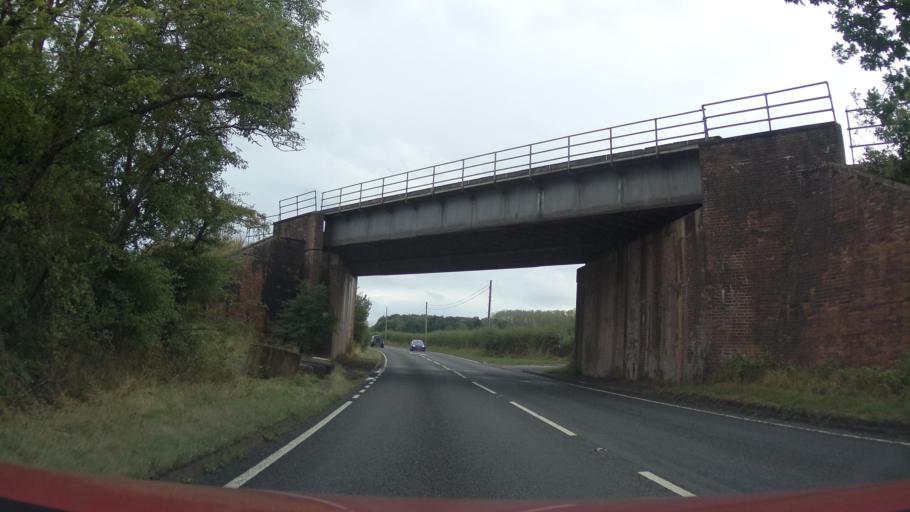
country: GB
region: England
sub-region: Worcestershire
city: Droitwich
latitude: 52.2999
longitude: -2.1752
